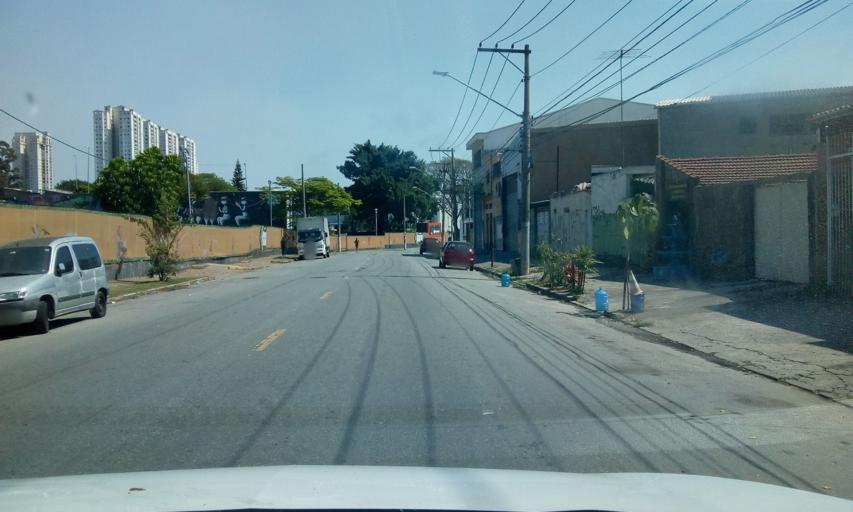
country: BR
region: Sao Paulo
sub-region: Osasco
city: Osasco
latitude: -23.5173
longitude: -46.7197
